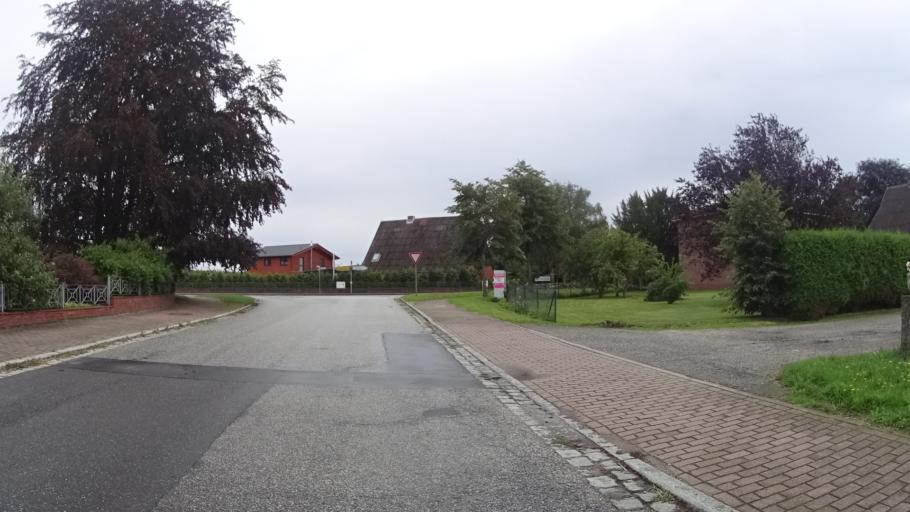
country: DE
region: Schleswig-Holstein
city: Stubben
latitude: 53.7196
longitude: 10.4084
